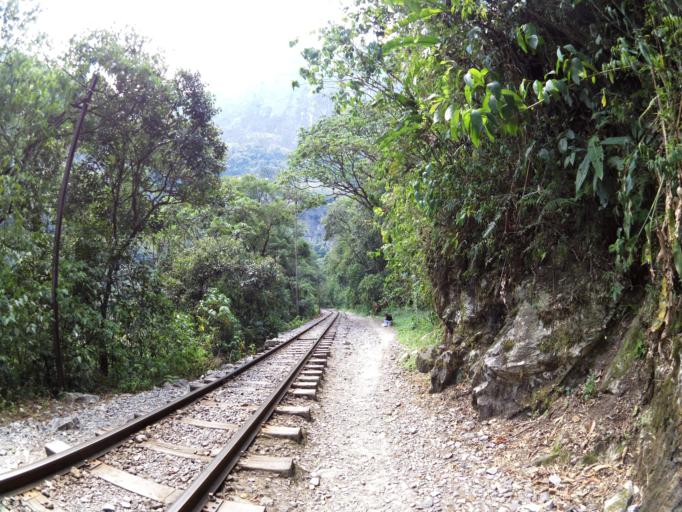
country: PE
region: Cusco
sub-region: Provincia de La Convencion
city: Santa Teresa
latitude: -13.1635
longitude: -72.5393
